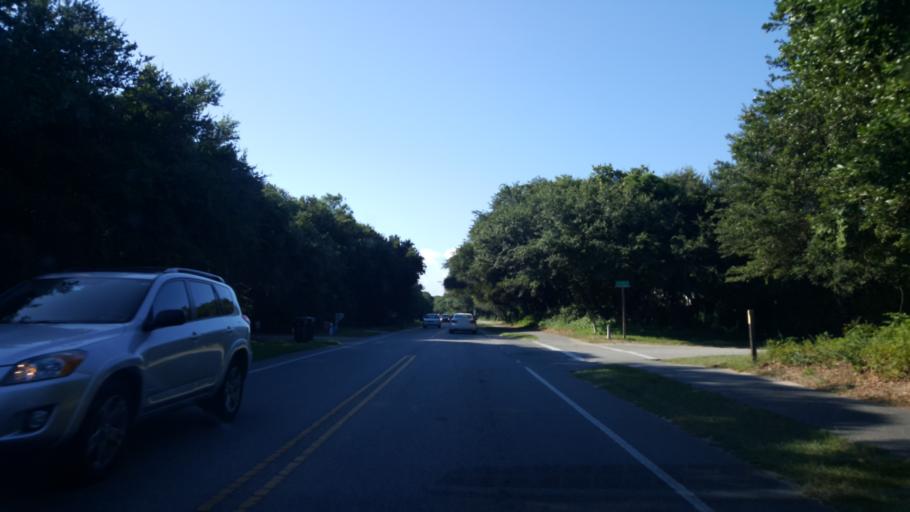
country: US
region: North Carolina
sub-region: Dare County
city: Southern Shores
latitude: 36.1381
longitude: -75.7362
